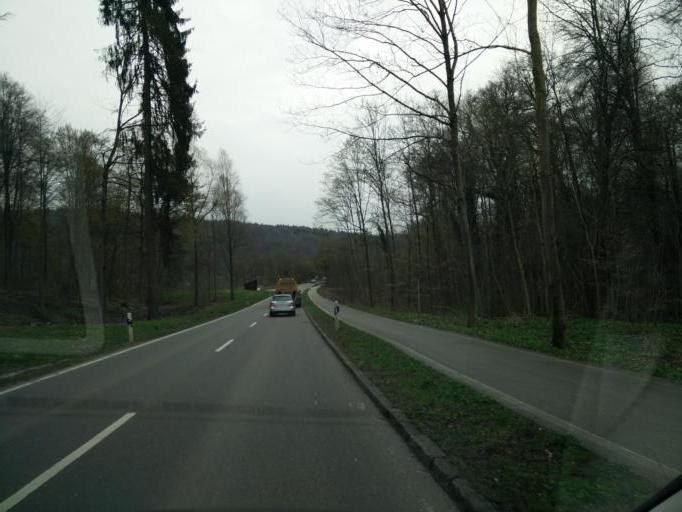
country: DE
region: Baden-Wuerttemberg
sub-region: Tuebingen Region
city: Kusterdingen
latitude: 48.5299
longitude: 9.1305
